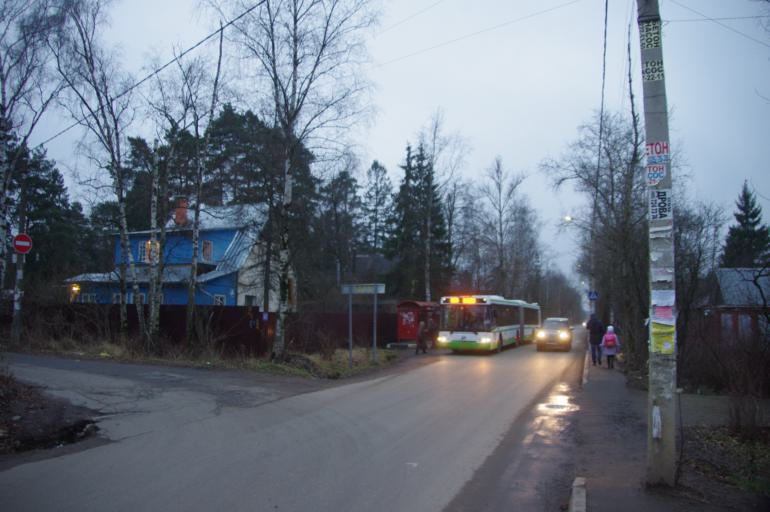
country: RU
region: Moskovskaya
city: Opalikha
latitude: 55.8303
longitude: 37.2491
